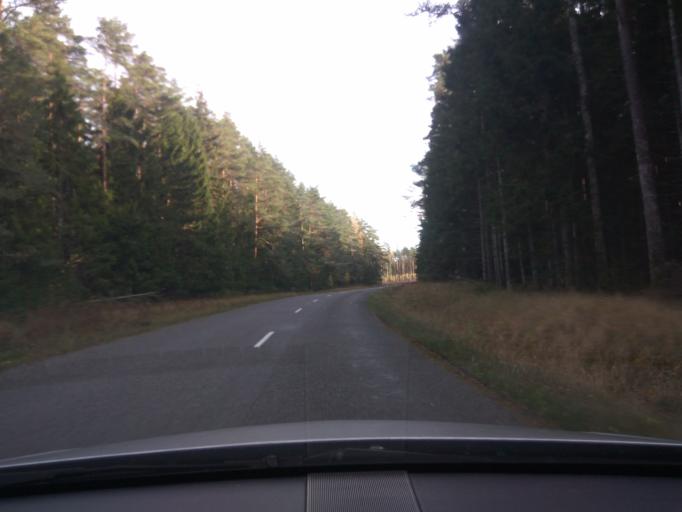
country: LV
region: Alsunga
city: Alsunga
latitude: 57.0141
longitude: 21.4160
